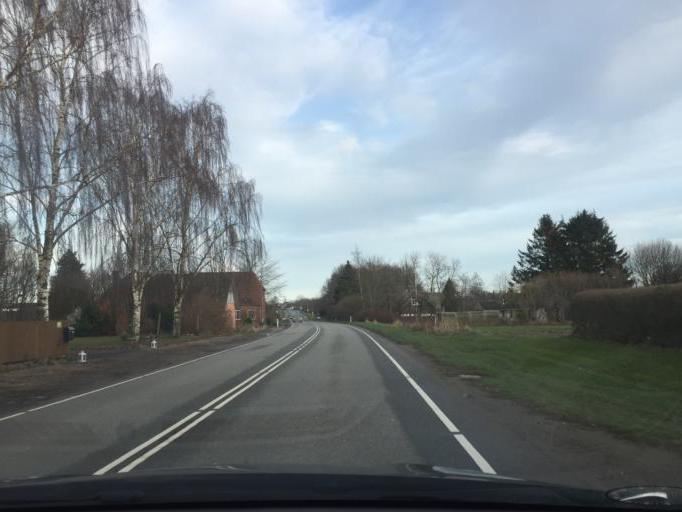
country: DK
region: South Denmark
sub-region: Faaborg-Midtfyn Kommune
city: Ringe
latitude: 55.2260
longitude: 10.4595
